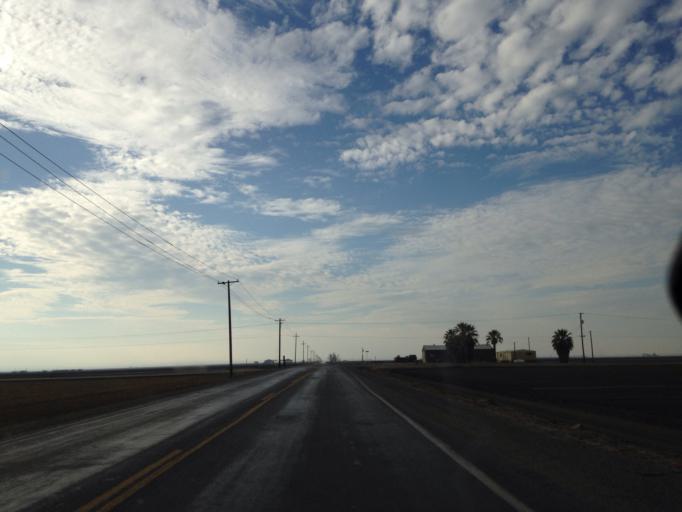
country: US
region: California
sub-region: Kern County
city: Buttonwillow
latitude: 35.4421
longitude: -119.5157
